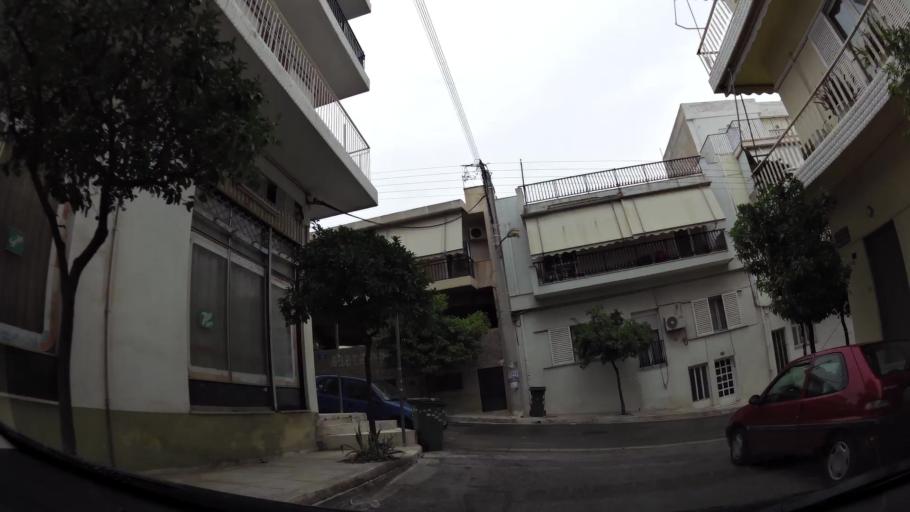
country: GR
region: Attica
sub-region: Nomos Piraios
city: Korydallos
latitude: 37.9868
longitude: 23.6495
